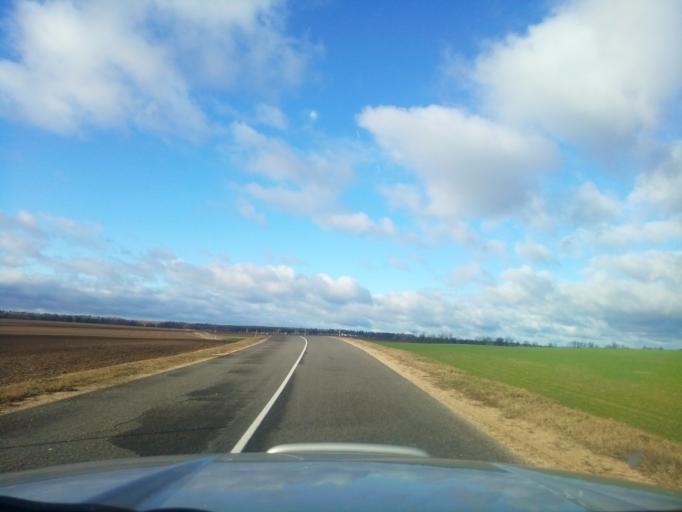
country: BY
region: Minsk
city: Kapyl'
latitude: 53.1682
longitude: 27.0545
